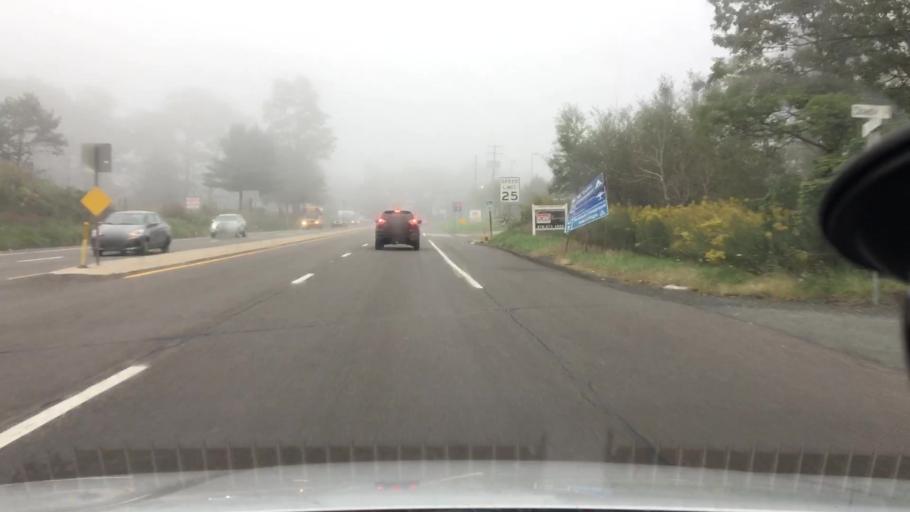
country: US
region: Pennsylvania
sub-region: Monroe County
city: Mount Pocono
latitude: 41.1259
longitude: -75.3627
